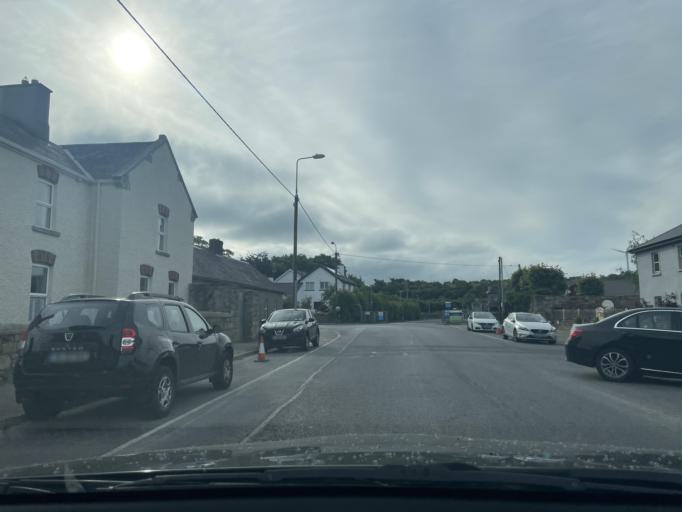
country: IE
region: Leinster
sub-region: County Carlow
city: Bagenalstown
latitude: 52.6999
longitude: -6.9541
